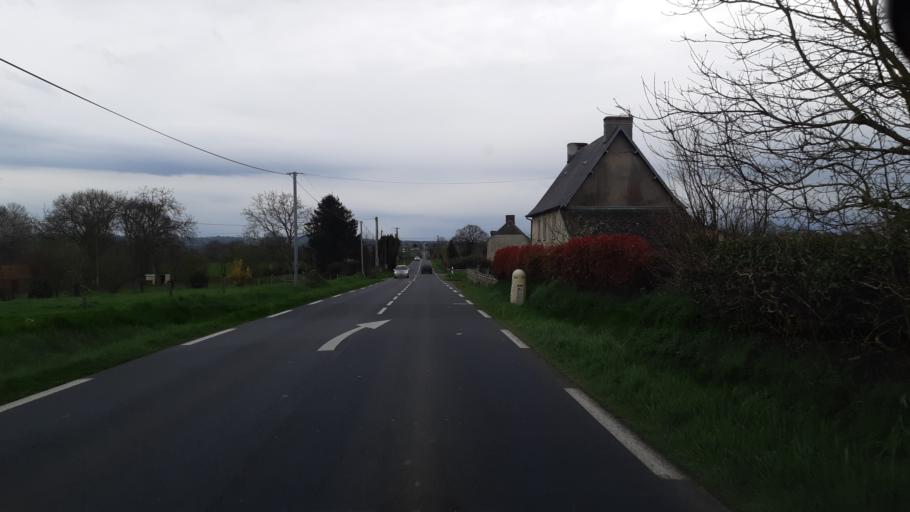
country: FR
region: Lower Normandy
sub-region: Departement de la Manche
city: Tessy-sur-Vire
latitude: 49.0108
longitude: -1.1502
